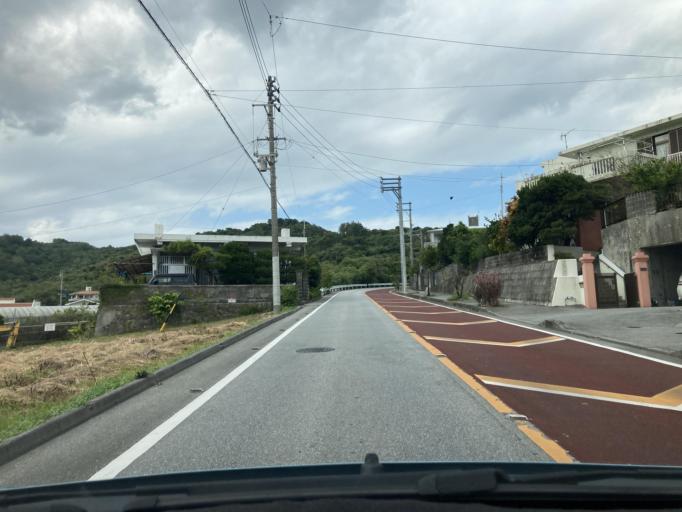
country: JP
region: Okinawa
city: Ginowan
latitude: 26.2561
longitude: 127.7840
